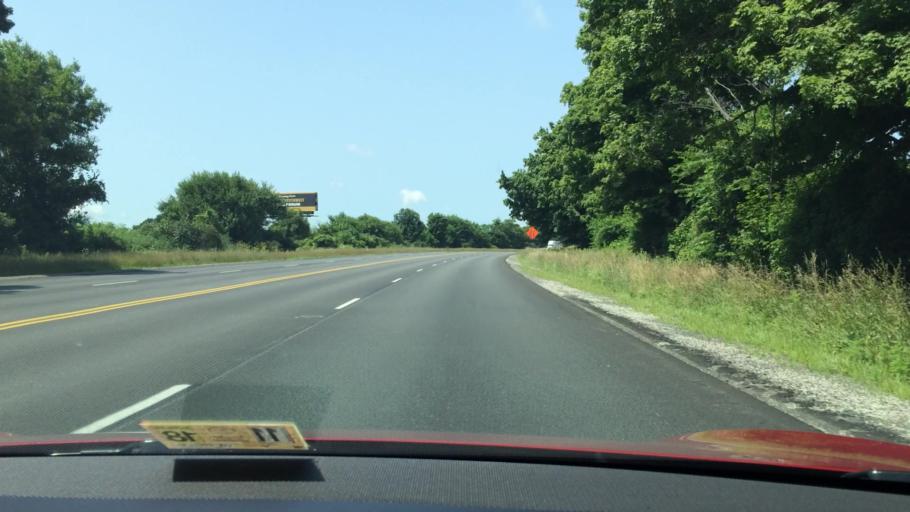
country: US
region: Indiana
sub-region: LaPorte County
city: Hudson Lake
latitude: 41.6707
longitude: -86.6049
